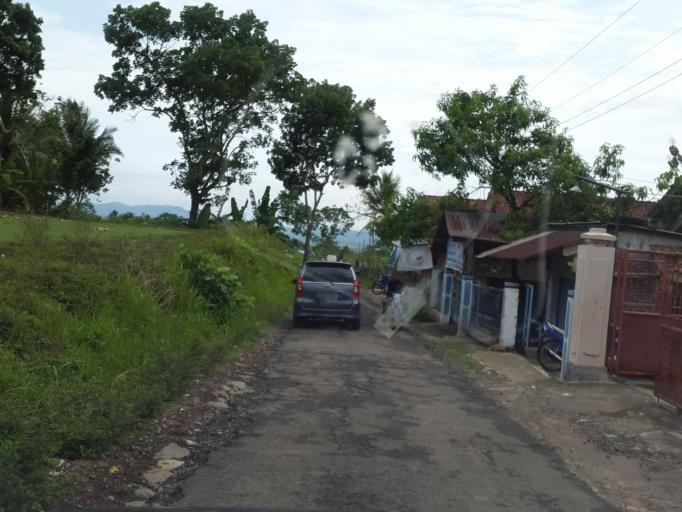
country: ID
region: Central Java
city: Baturaden
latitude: -7.3585
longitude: 109.2170
